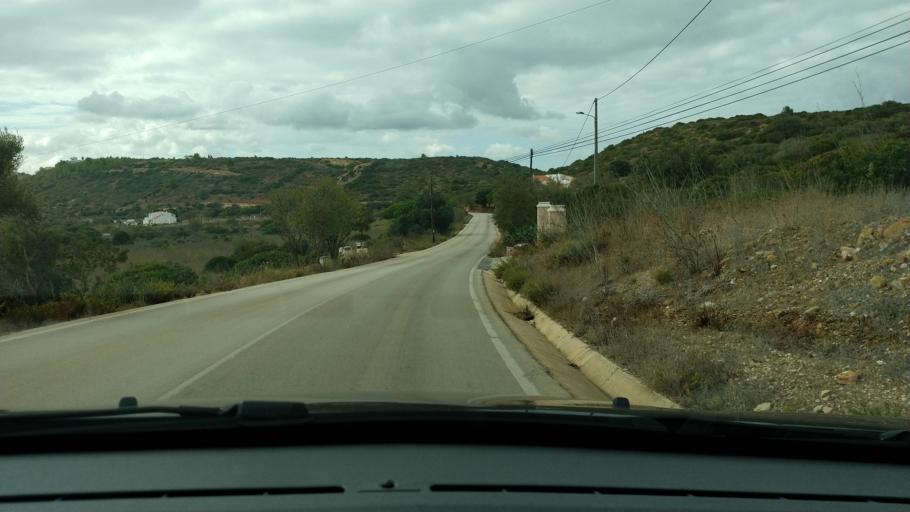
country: PT
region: Faro
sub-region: Lagos
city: Lagos
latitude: 37.0704
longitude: -8.7871
